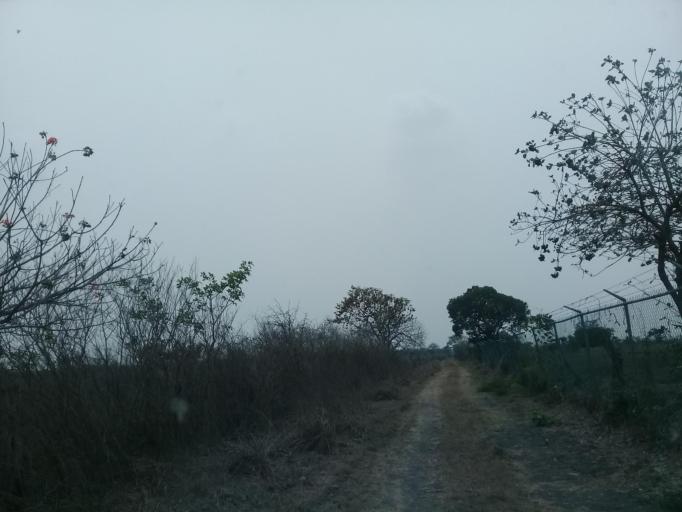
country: MX
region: Veracruz
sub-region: Medellin
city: La Laguna y Monte del Castillo
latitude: 18.9065
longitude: -96.1292
